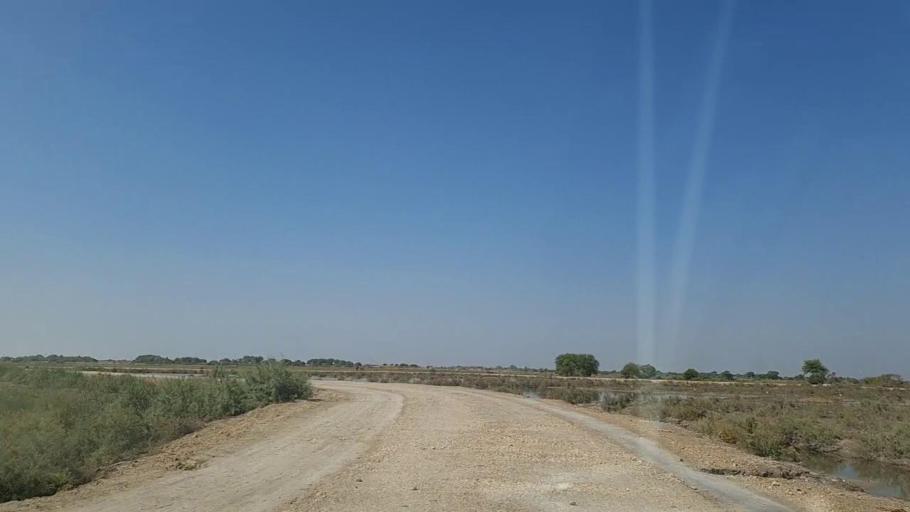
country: PK
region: Sindh
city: Chuhar Jamali
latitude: 24.4242
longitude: 68.0102
